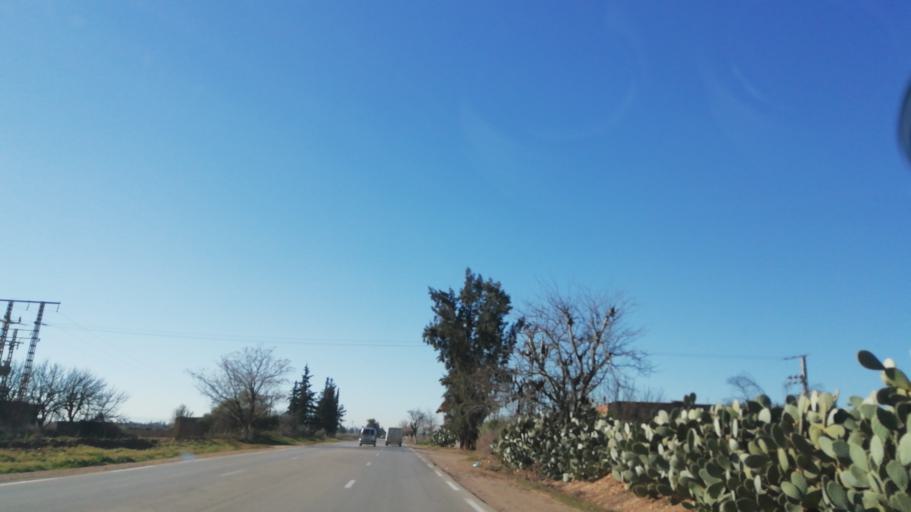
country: MA
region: Oriental
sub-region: Oujda-Angad
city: Oujda
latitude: 34.8191
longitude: -1.8035
